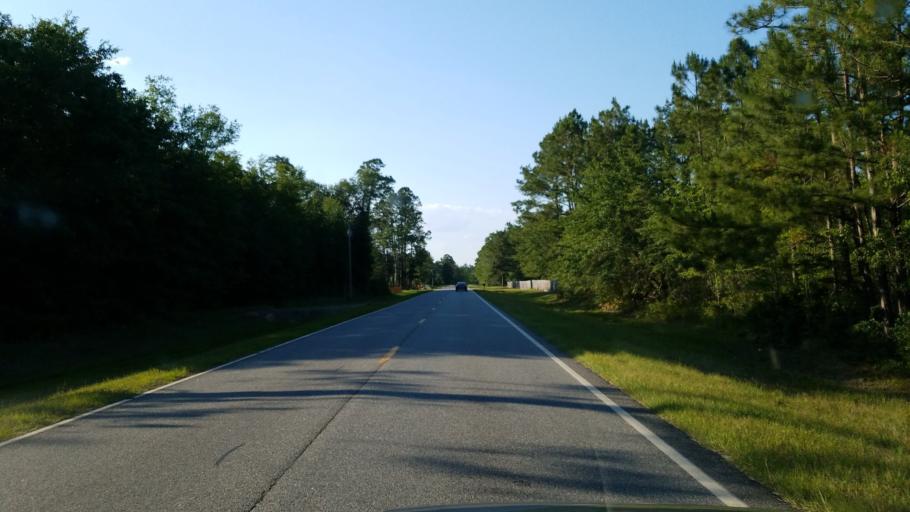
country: US
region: Georgia
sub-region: Lanier County
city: Lakeland
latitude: 30.9220
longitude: -83.0803
